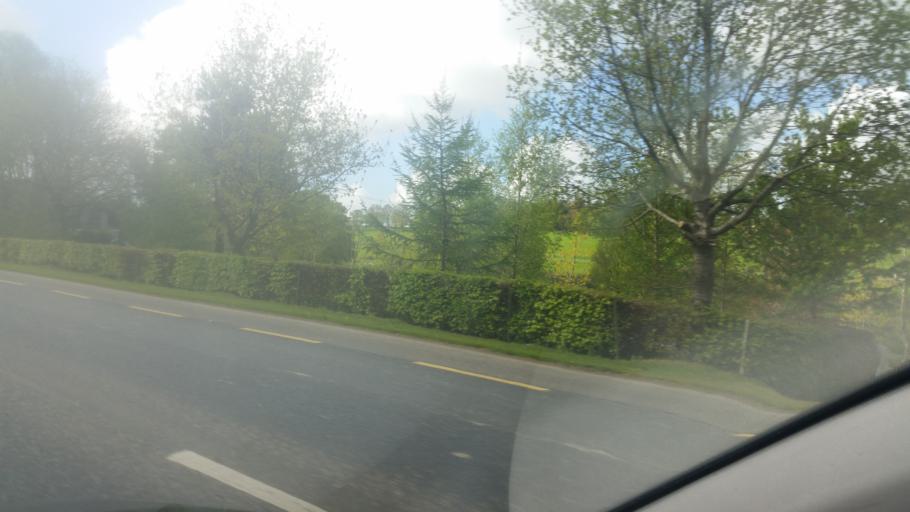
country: IE
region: Leinster
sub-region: Loch Garman
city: Enniscorthy
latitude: 52.4639
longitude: -6.5603
